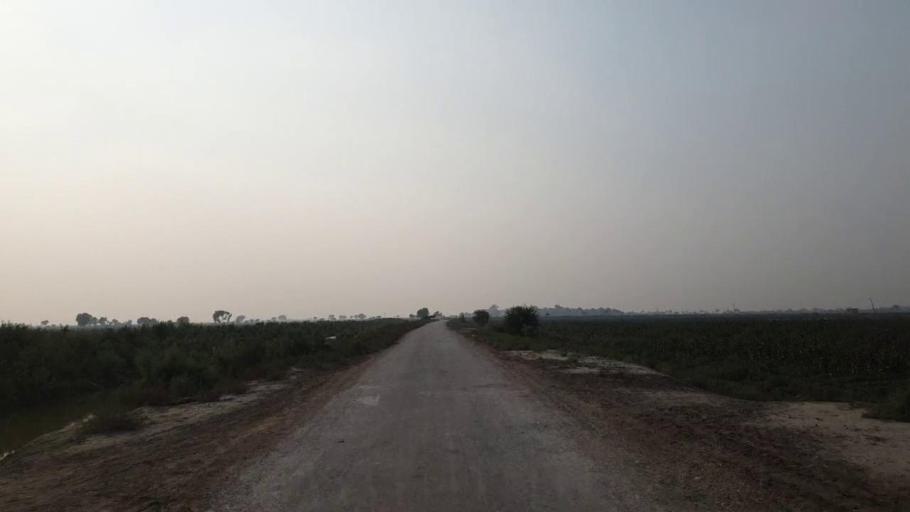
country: PK
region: Sindh
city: Bhan
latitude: 26.4884
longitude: 67.7147
